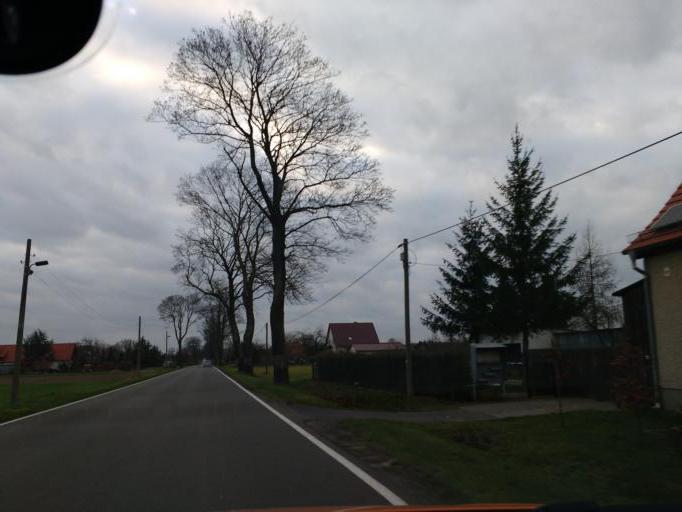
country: DE
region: Brandenburg
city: Wriezen
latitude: 52.6706
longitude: 14.0666
